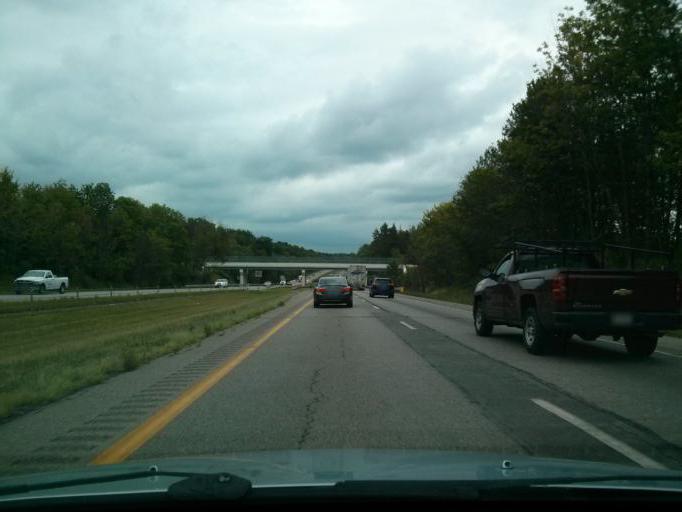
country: US
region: Ohio
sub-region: Portage County
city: Ravenna
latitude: 41.1060
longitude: -81.1959
